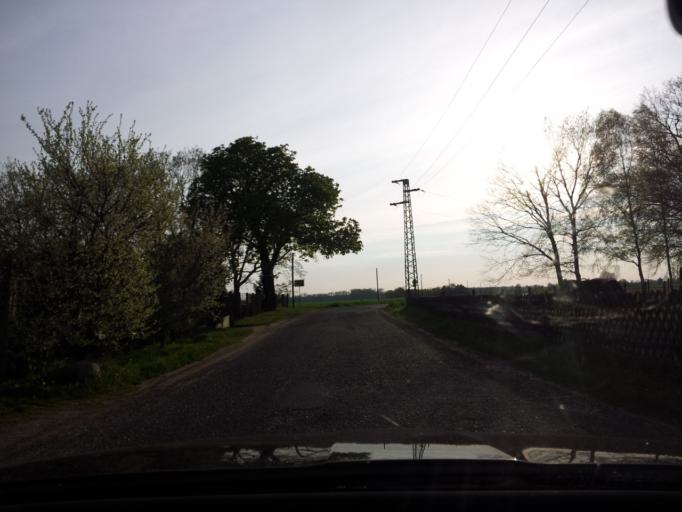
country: DE
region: Brandenburg
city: Dahme
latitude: 51.8537
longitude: 13.4360
